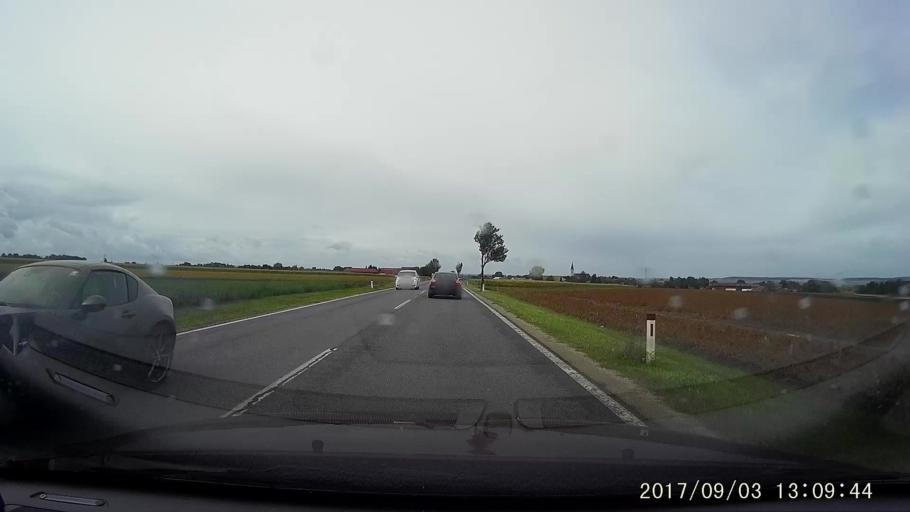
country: AT
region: Lower Austria
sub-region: Politischer Bezirk Hollabrunn
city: Hollabrunn
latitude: 48.5943
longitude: 16.0651
